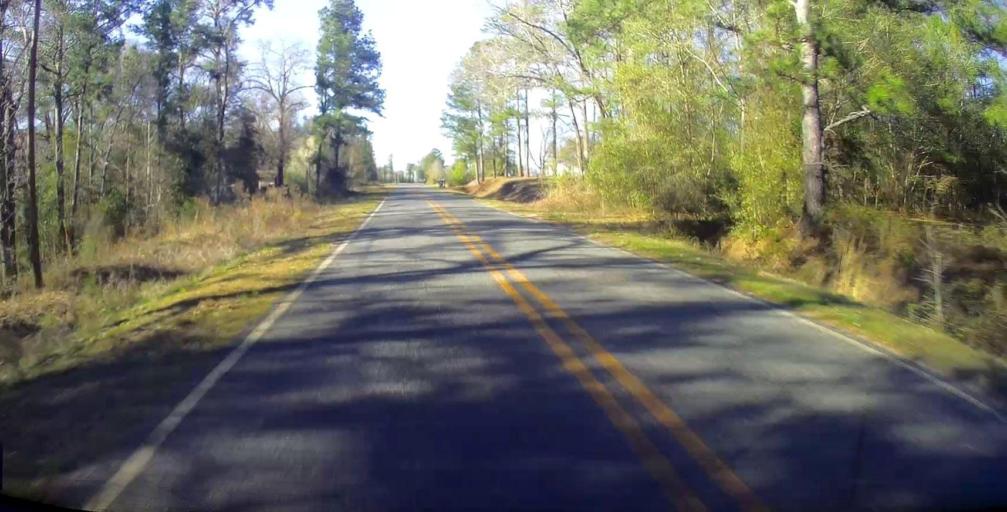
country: US
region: Georgia
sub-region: Peach County
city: Fort Valley
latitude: 32.5891
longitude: -83.8514
